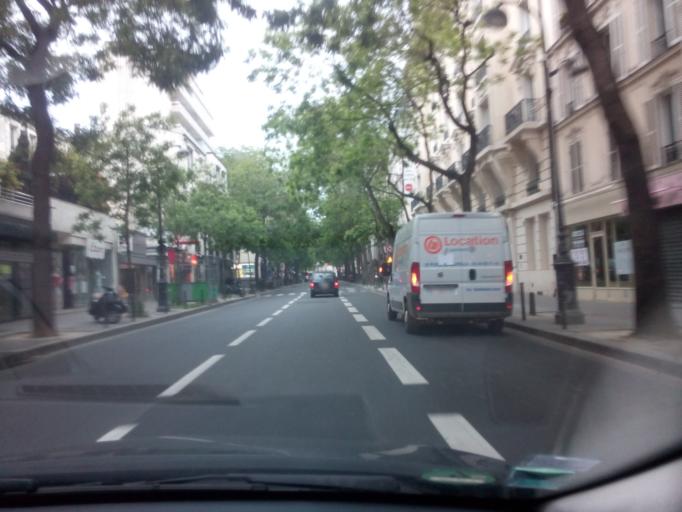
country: FR
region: Ile-de-France
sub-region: Departement des Hauts-de-Seine
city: Montrouge
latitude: 48.8290
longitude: 2.3236
